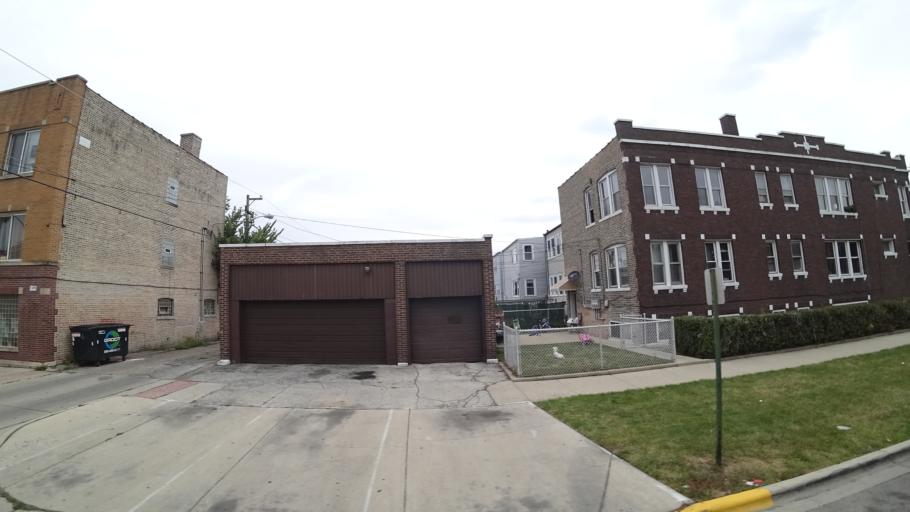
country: US
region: Illinois
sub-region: Cook County
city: Cicero
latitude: 41.8567
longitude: -87.7461
